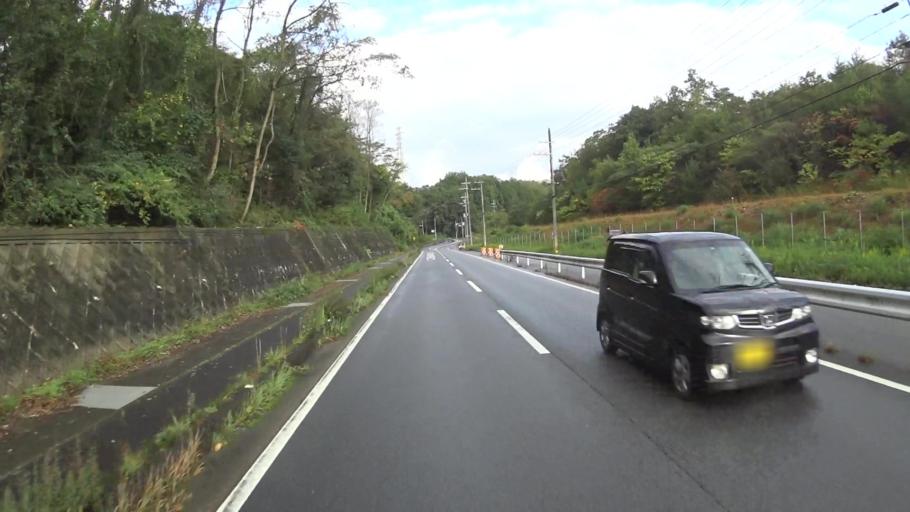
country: JP
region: Kyoto
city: Fukuchiyama
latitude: 35.2872
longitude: 135.1788
